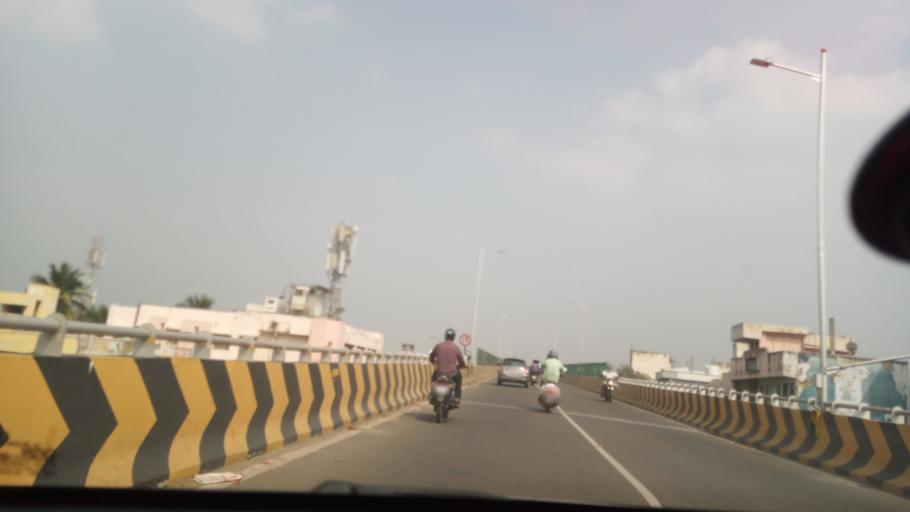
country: IN
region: Tamil Nadu
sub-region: Coimbatore
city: Coimbatore
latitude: 11.0203
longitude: 76.9684
